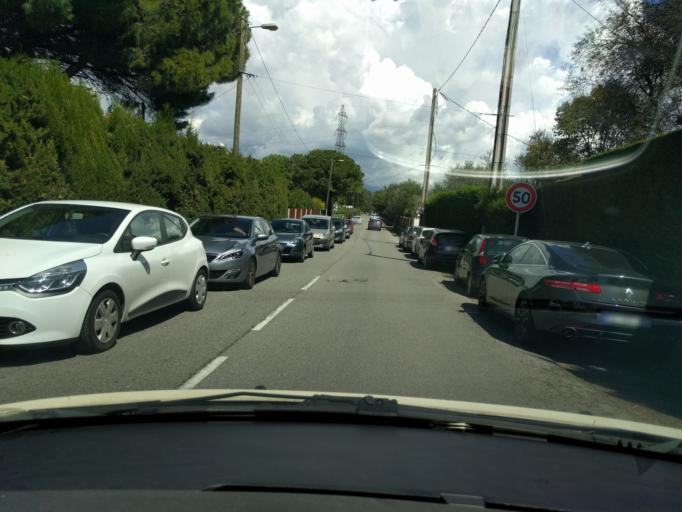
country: FR
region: Provence-Alpes-Cote d'Azur
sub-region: Departement des Alpes-Maritimes
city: La Roquette-sur-Siagne
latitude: 43.5997
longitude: 6.9574
